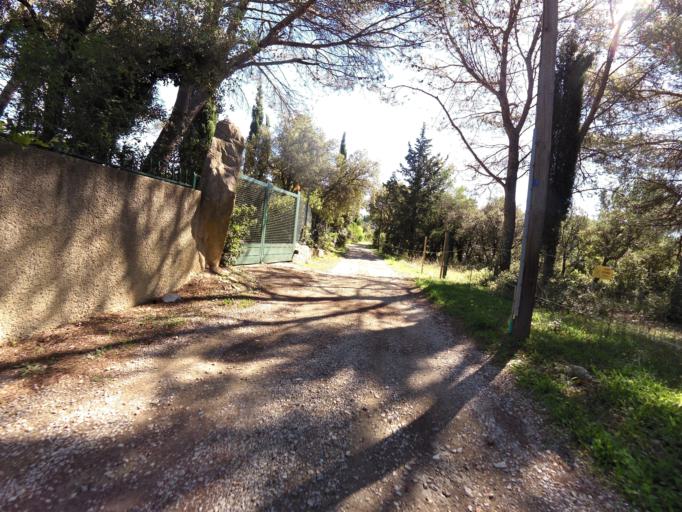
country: FR
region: Languedoc-Roussillon
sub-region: Departement du Gard
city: Aubais
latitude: 43.7490
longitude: 4.1449
